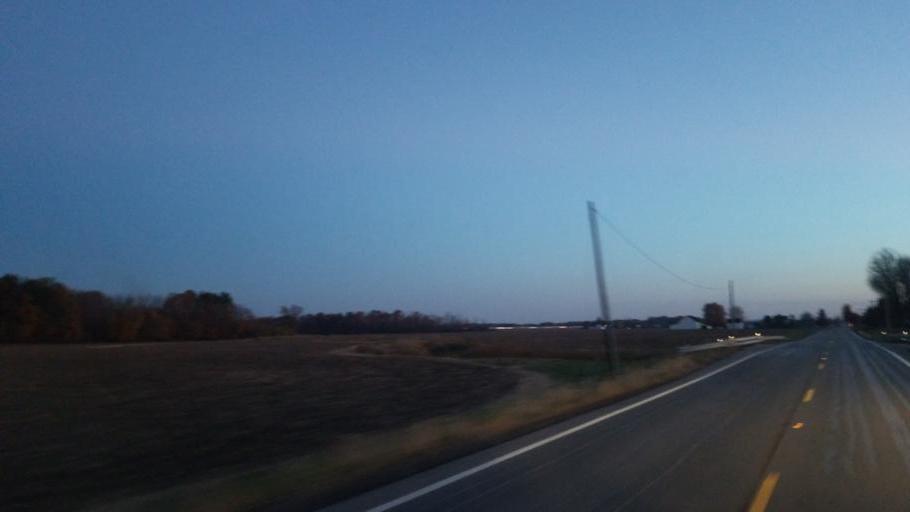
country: US
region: Ohio
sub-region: Crawford County
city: Crestline
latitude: 40.8211
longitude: -82.7302
